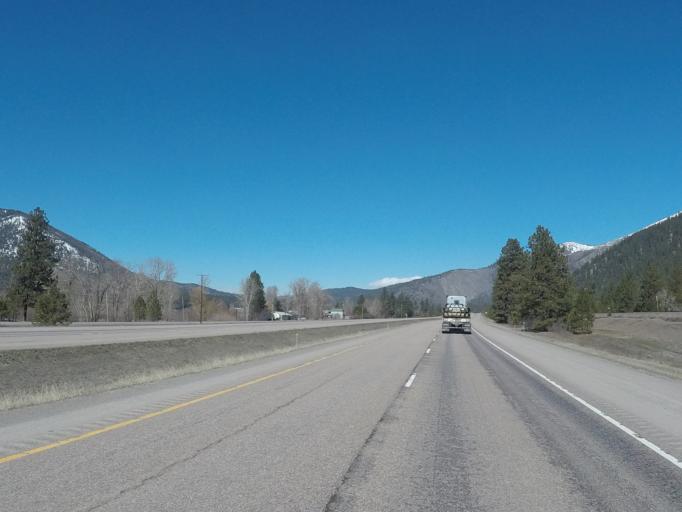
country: US
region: Montana
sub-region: Missoula County
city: Bonner-West Riverside
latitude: 46.8532
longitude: -113.8554
